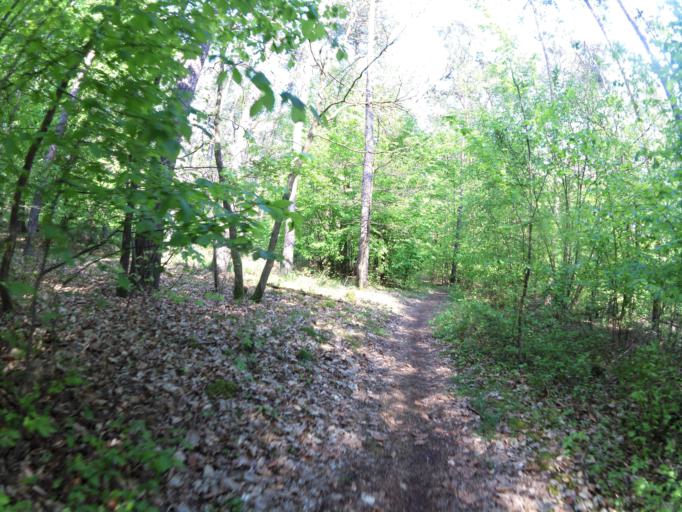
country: DE
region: Bavaria
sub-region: Regierungsbezirk Unterfranken
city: Sommerhausen
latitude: 49.7020
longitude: 10.0477
